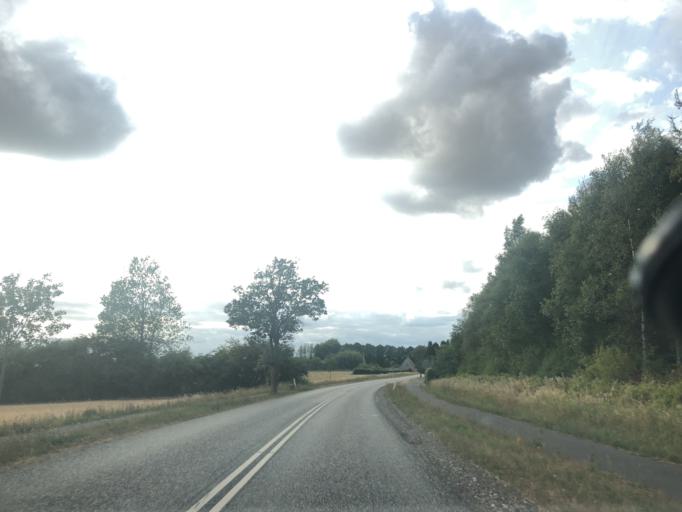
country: DK
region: Zealand
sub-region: Koge Kommune
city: Bjaeverskov
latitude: 55.4230
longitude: 12.0009
